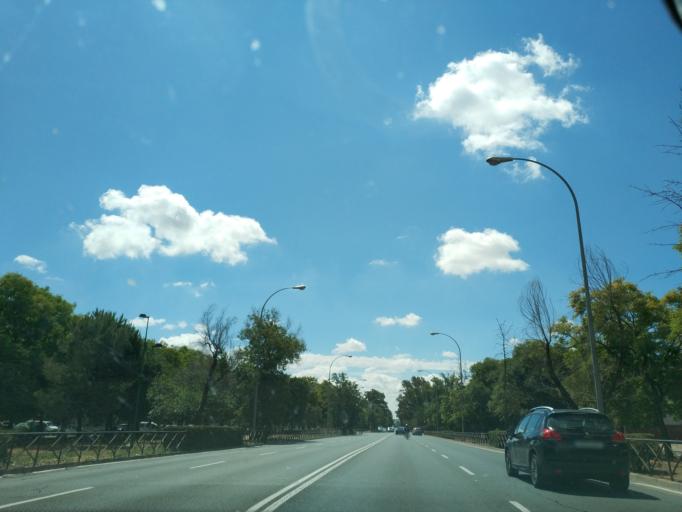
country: ES
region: Andalusia
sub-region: Provincia de Sevilla
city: Sevilla
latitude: 37.3663
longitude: -5.9655
